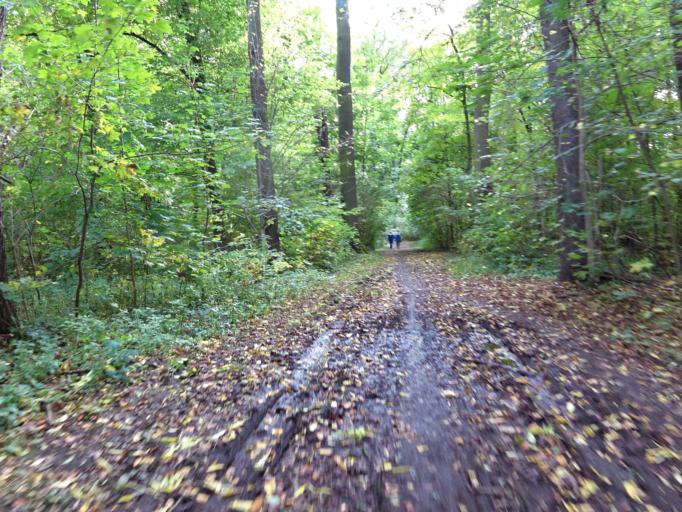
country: DE
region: Saxony
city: Leipzig
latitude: 51.3140
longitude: 12.3532
